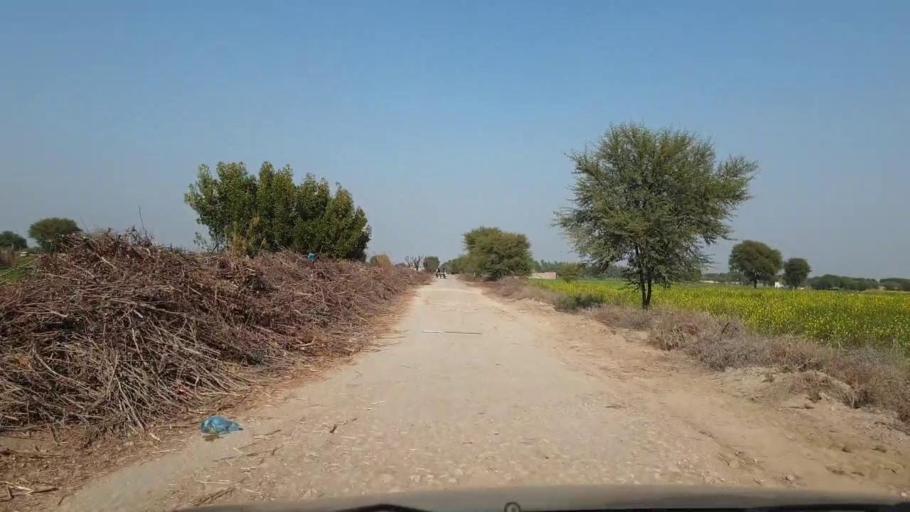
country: PK
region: Sindh
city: Jhol
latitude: 25.9380
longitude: 68.8803
